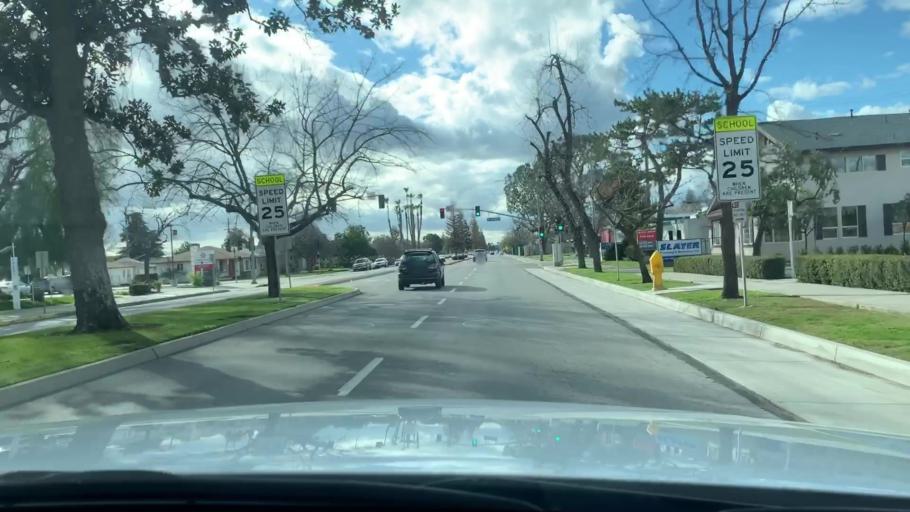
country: US
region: California
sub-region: Kern County
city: Bakersfield
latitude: 35.3734
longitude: -119.0285
